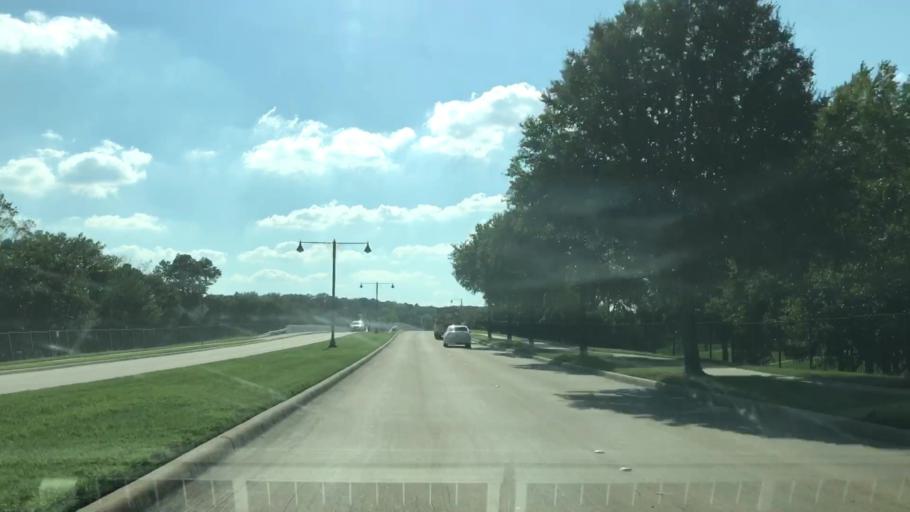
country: US
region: Texas
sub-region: Tarrant County
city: Colleyville
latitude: 32.9219
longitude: -97.1946
